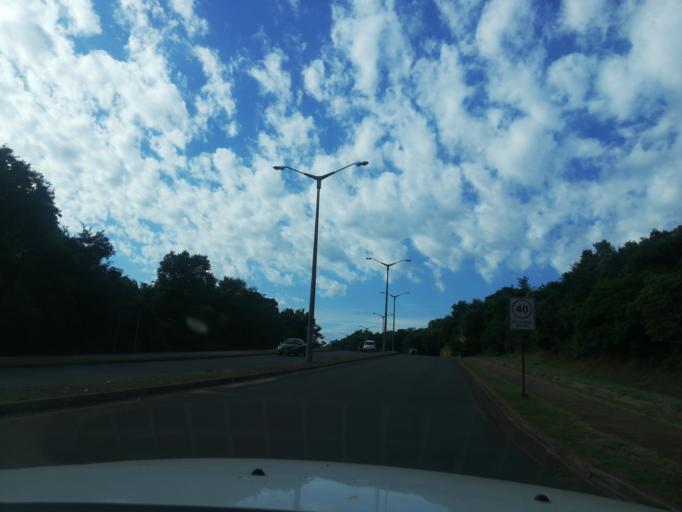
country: PY
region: Itapua
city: Encarnacion
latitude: -27.3439
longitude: -55.8535
